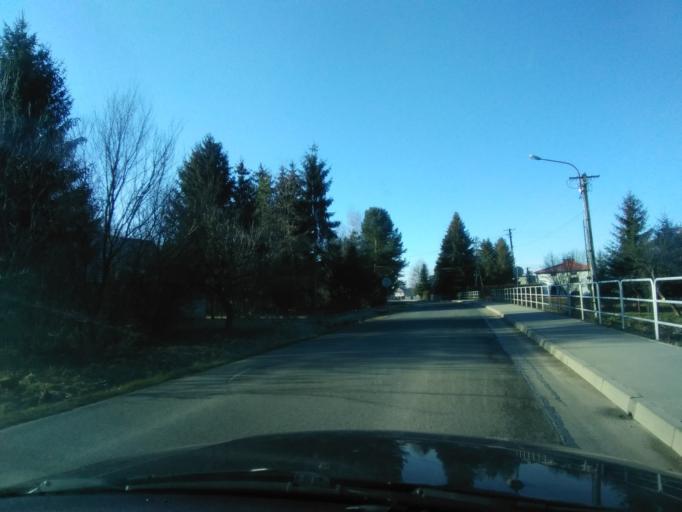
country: PL
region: Subcarpathian Voivodeship
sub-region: Powiat brzozowski
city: Haczow
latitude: 49.6773
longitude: 21.8753
